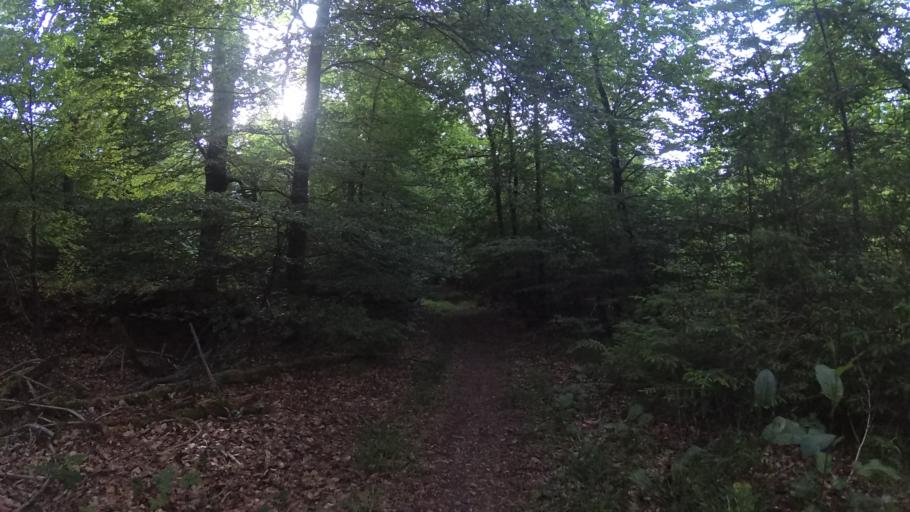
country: DE
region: Saarland
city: Sankt Wendel
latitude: 49.4353
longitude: 7.1949
